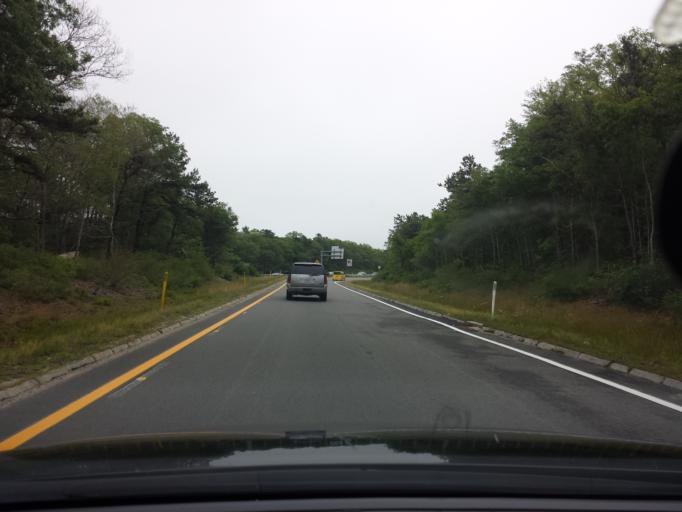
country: US
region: Massachusetts
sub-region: Barnstable County
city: Sagamore
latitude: 41.7683
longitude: -70.5449
